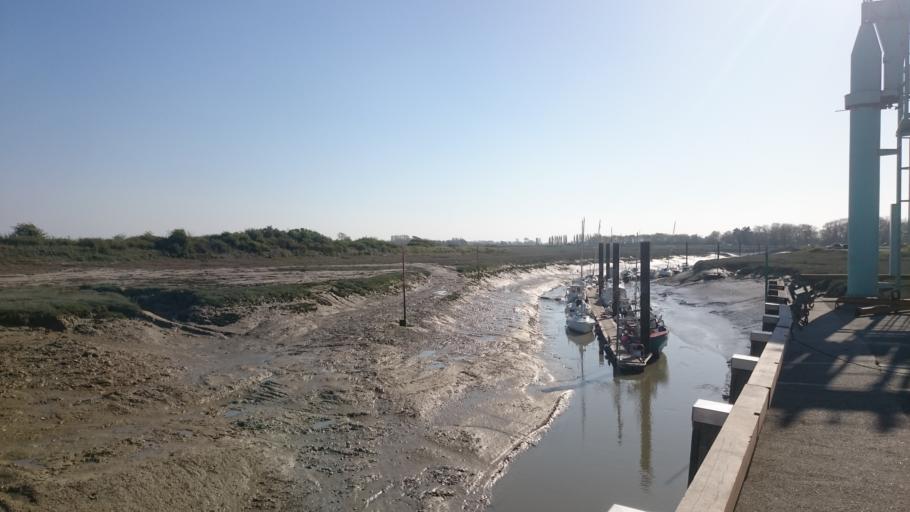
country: FR
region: Picardie
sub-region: Departement de la Somme
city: Pende
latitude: 50.2141
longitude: 1.5643
